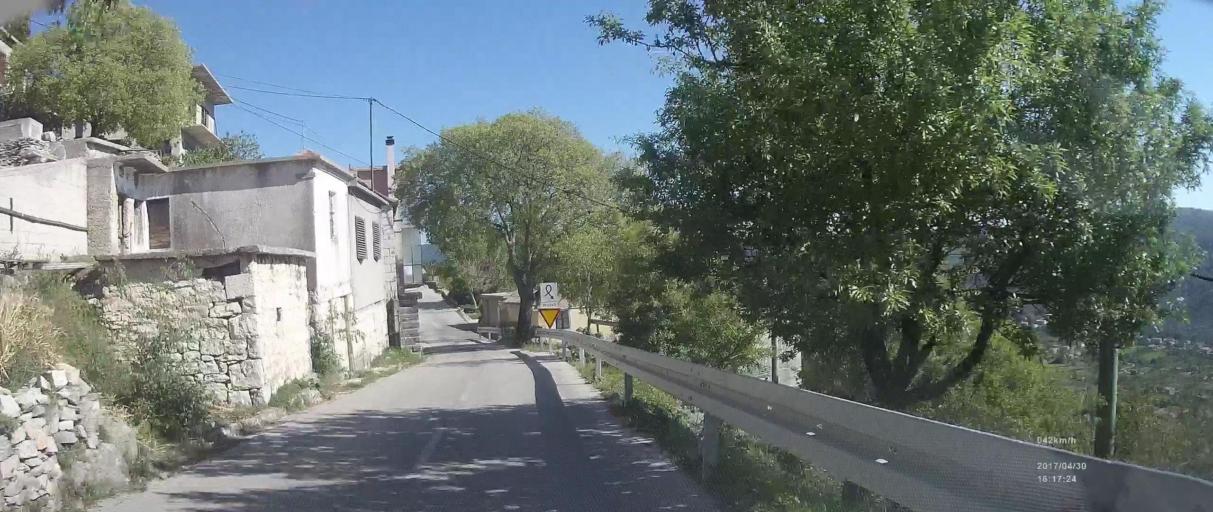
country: HR
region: Splitsko-Dalmatinska
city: Srinjine
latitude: 43.4991
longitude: 16.6101
